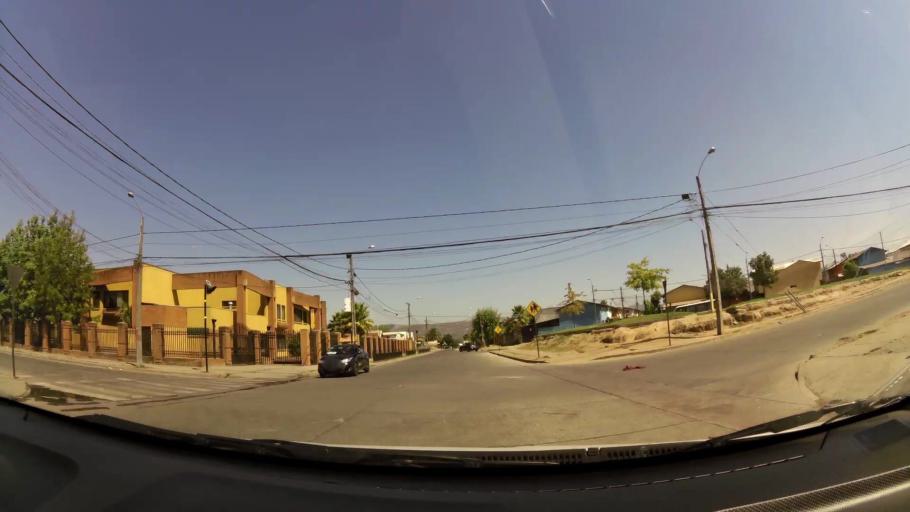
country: CL
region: Maule
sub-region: Provincia de Talca
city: Talca
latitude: -35.4191
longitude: -71.6404
